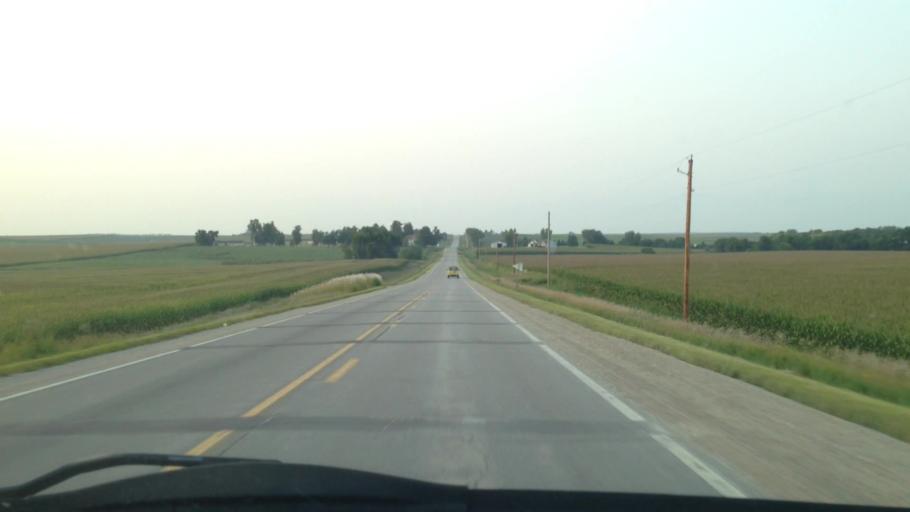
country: US
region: Iowa
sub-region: Benton County
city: Atkins
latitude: 41.9995
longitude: -91.8734
